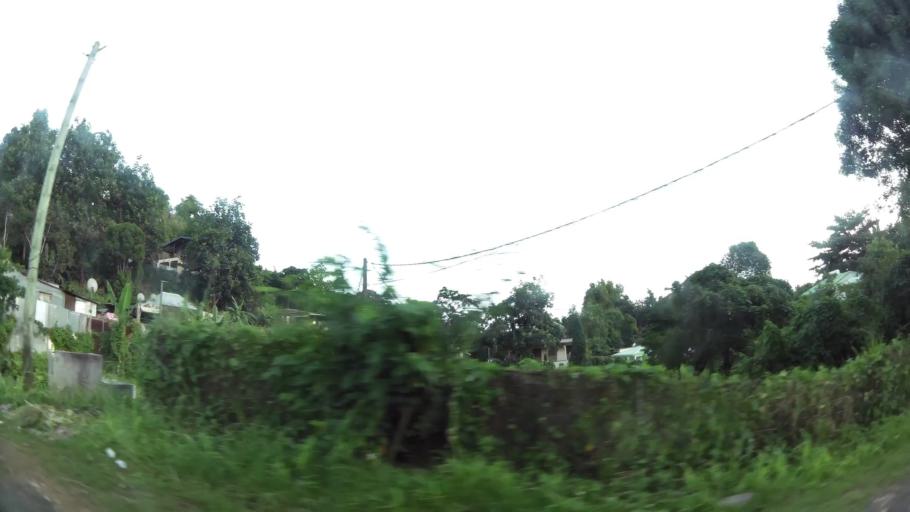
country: GP
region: Guadeloupe
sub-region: Guadeloupe
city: Les Abymes
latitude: 16.2646
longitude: -61.4996
